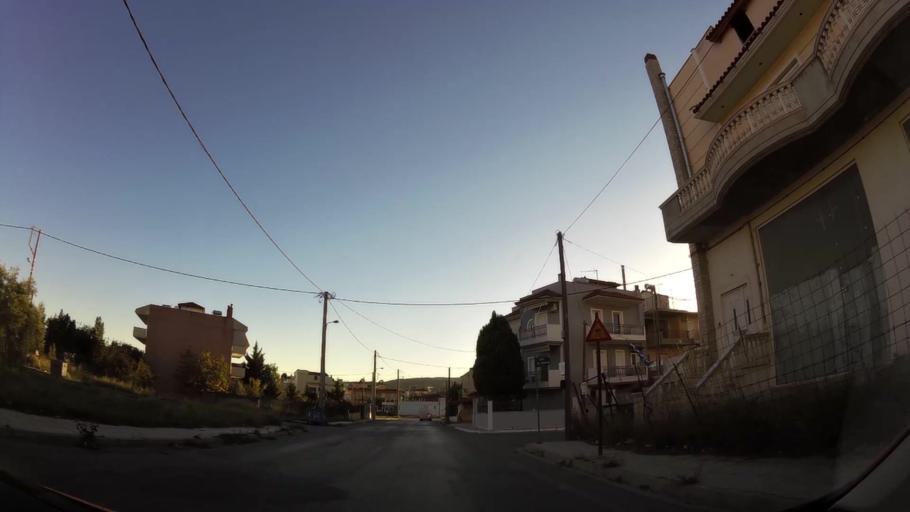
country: GR
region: Attica
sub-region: Nomarchia Dytikis Attikis
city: Ano Liosia
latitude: 38.0882
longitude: 23.7150
